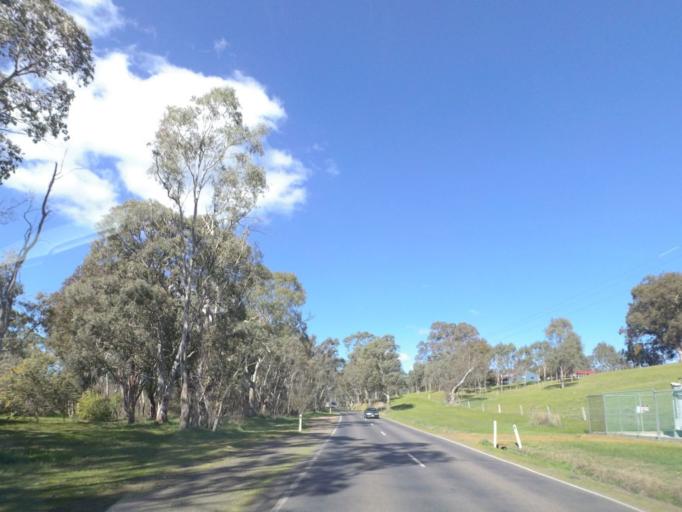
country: AU
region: Victoria
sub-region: Murrindindi
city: Alexandra
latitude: -37.1924
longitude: 145.7256
